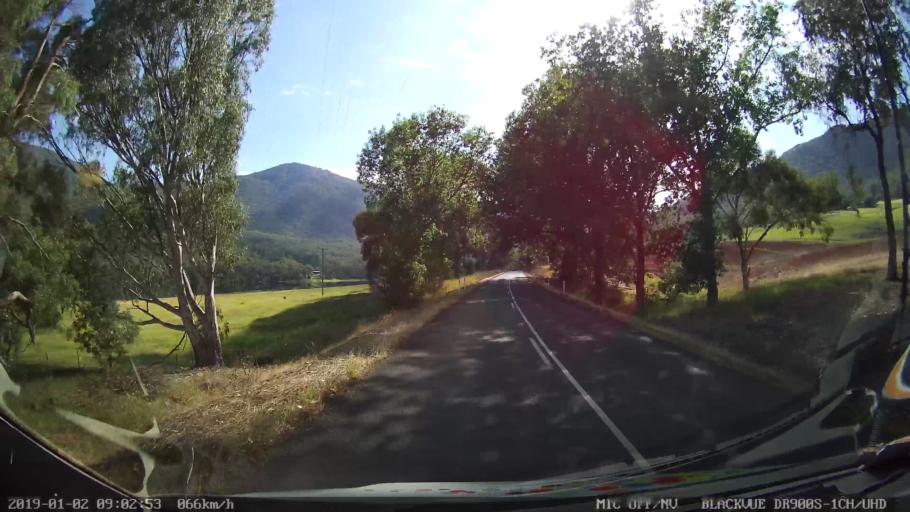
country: AU
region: New South Wales
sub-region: Tumut Shire
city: Tumut
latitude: -35.5700
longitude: 148.3168
